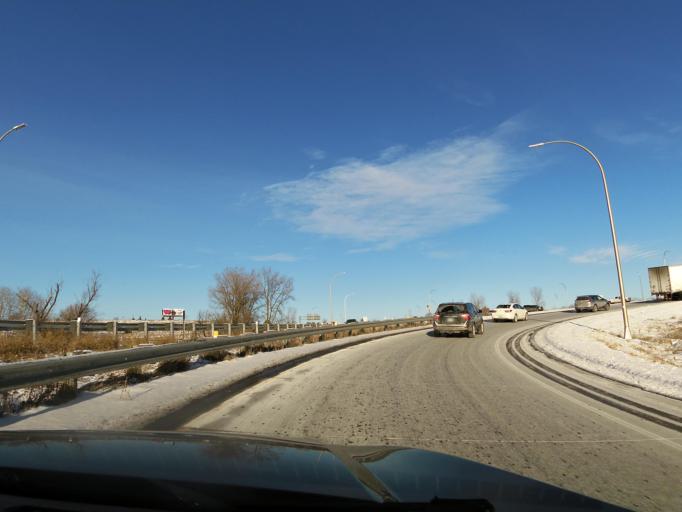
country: US
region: Minnesota
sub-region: Washington County
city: Oakdale
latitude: 44.9501
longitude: -92.9612
